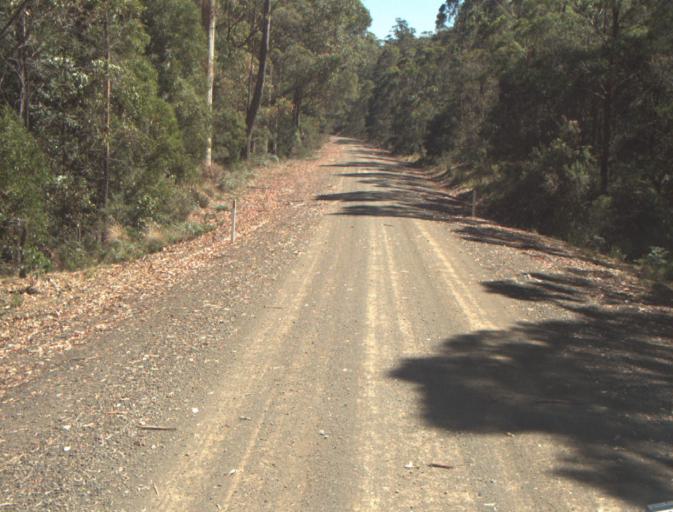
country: AU
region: Tasmania
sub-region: Launceston
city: Newstead
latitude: -41.3069
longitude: 147.3346
